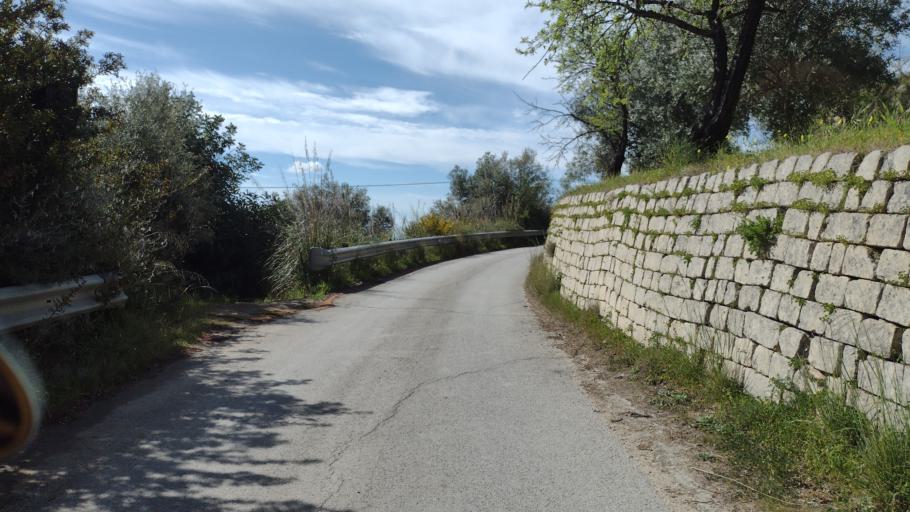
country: IT
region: Sicily
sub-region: Provincia di Siracusa
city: Noto
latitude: 36.9071
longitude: 15.0262
